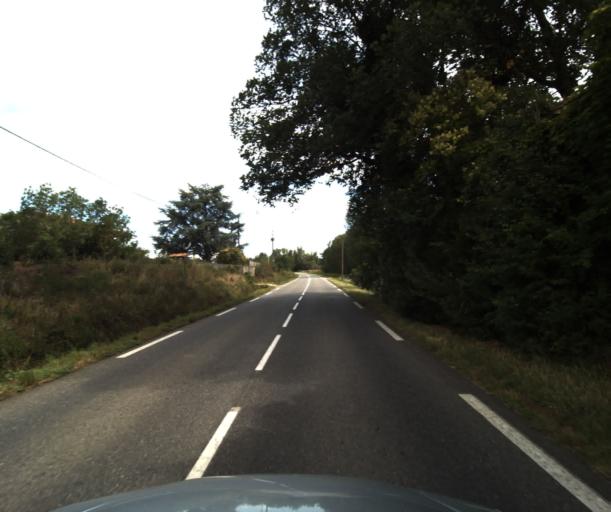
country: FR
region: Midi-Pyrenees
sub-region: Departement de la Haute-Garonne
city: Seysses
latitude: 43.4735
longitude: 1.3032
